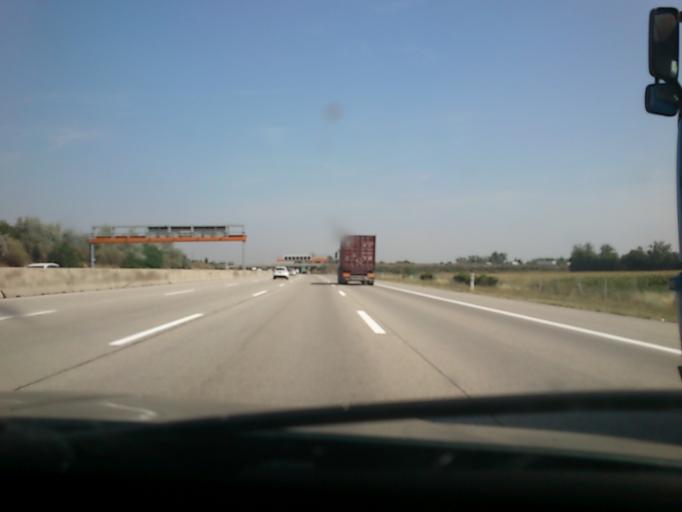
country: AT
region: Lower Austria
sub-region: Politischer Bezirk Modling
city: Guntramsdorf
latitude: 48.0249
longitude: 16.3337
